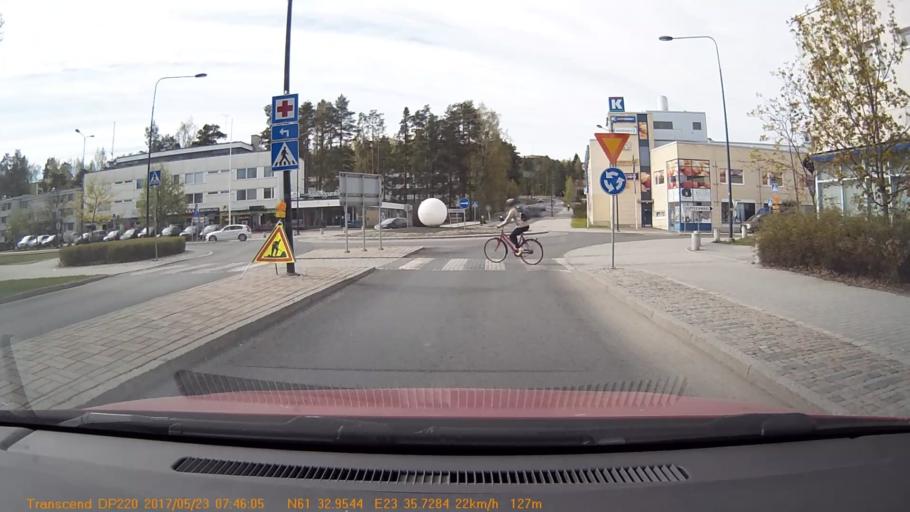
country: FI
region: Pirkanmaa
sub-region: Tampere
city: Yloejaervi
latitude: 61.5493
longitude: 23.5954
